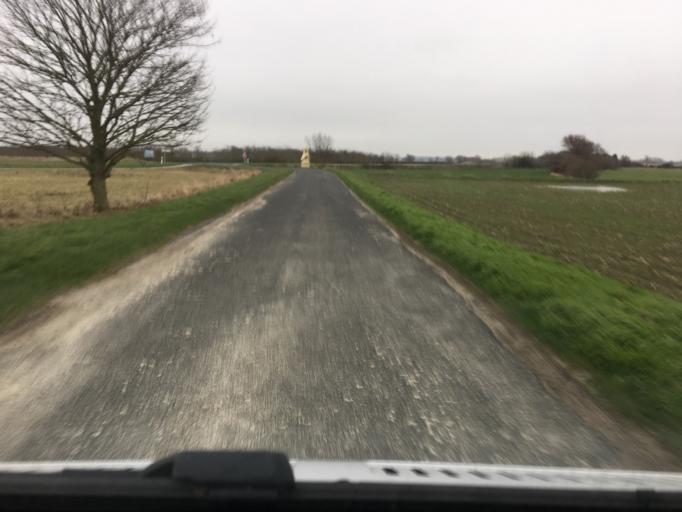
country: FR
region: Picardie
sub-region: Departement de la Somme
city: Pende
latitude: 50.1946
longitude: 1.5568
